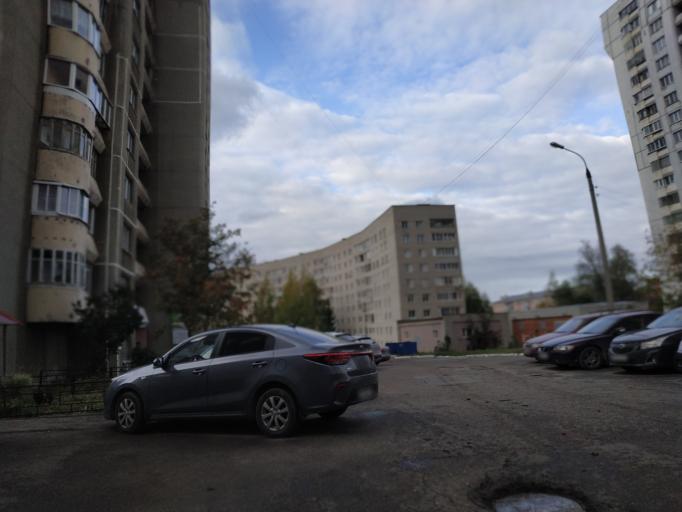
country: RU
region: Chuvashia
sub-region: Cheboksarskiy Rayon
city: Cheboksary
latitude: 56.1465
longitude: 47.2169
